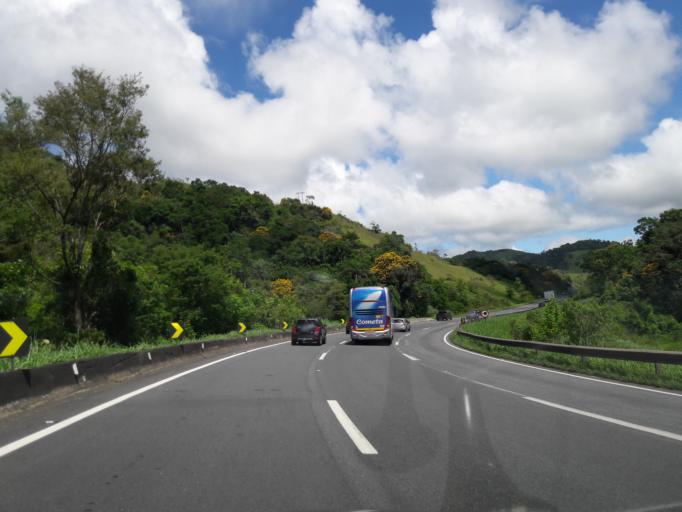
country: BR
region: Sao Paulo
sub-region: Cajati
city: Cajati
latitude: -24.9612
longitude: -48.4667
